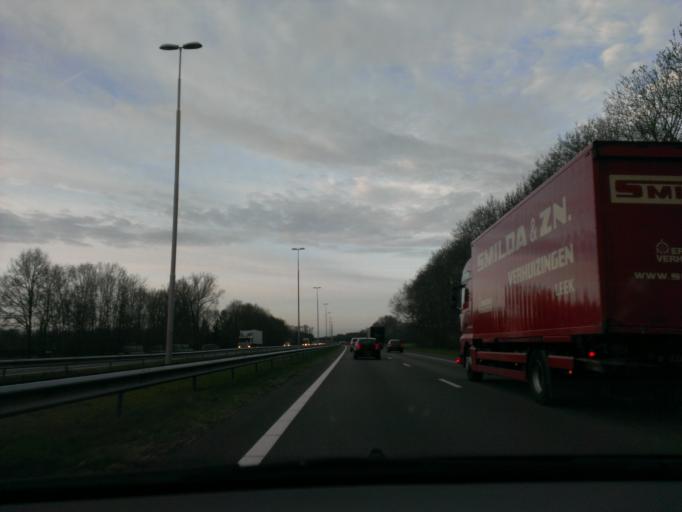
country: NL
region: Gelderland
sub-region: Gemeente Epe
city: Oene
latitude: 52.3510
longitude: 6.0191
